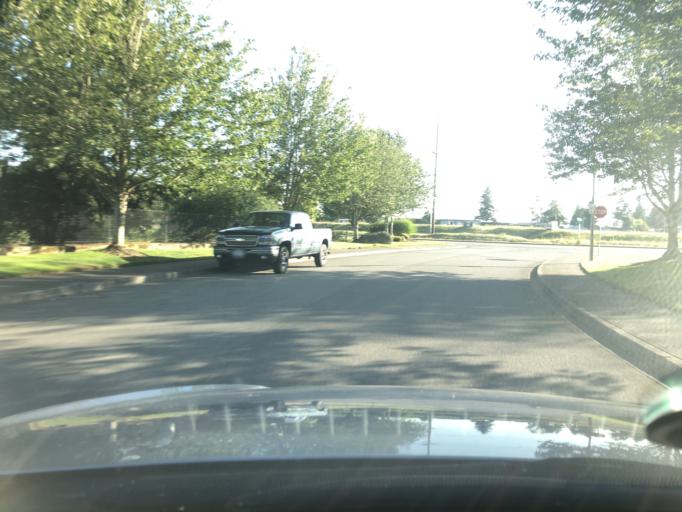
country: US
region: Washington
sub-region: Pierce County
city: Bonney Lake
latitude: 47.2312
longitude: -122.1436
